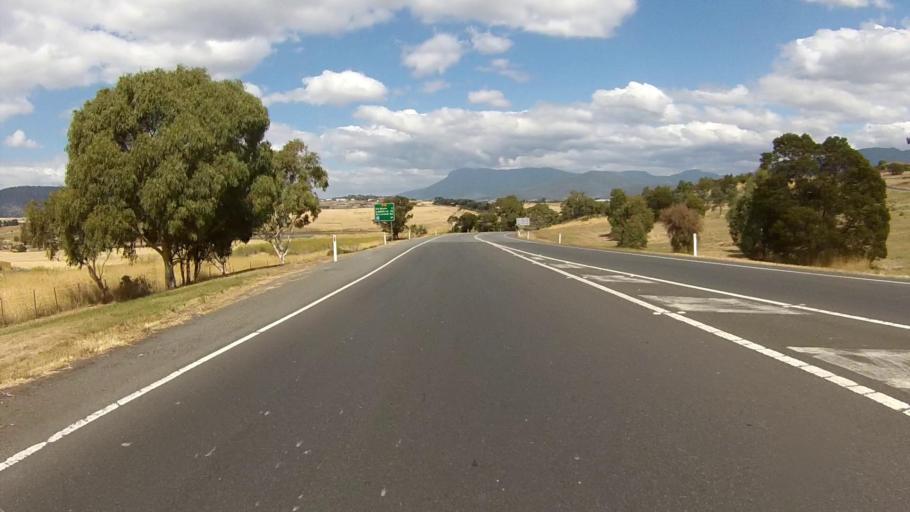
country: AU
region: Tasmania
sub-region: Brighton
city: Old Beach
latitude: -42.7515
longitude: 147.2725
